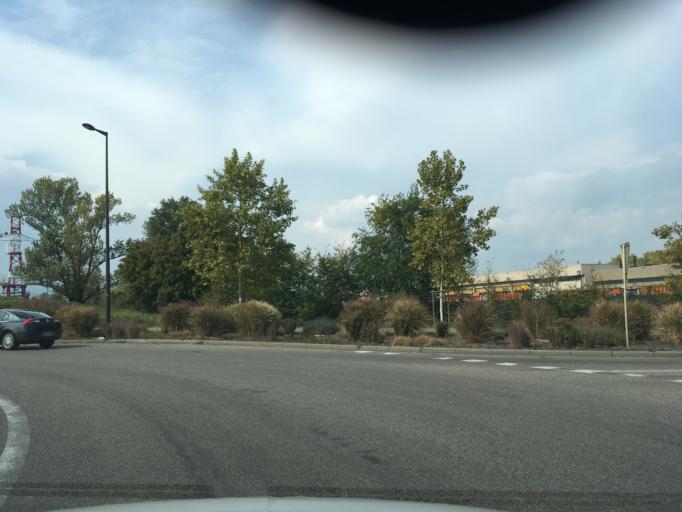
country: FR
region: Alsace
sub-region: Departement du Haut-Rhin
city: Colmar
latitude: 48.0934
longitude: 7.3559
